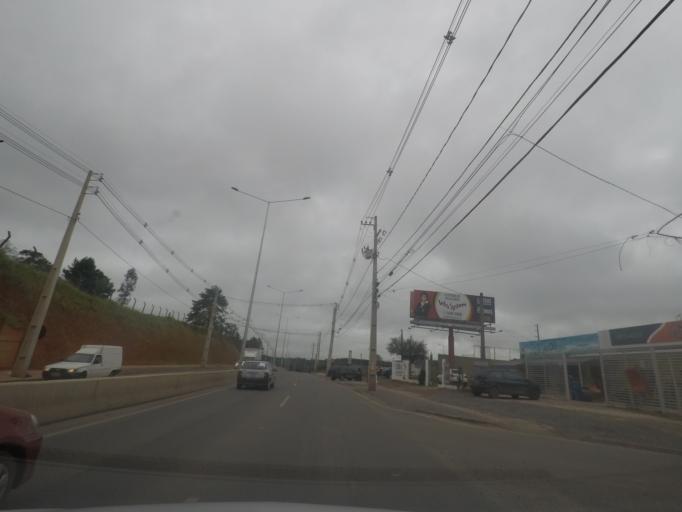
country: BR
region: Parana
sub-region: Piraquara
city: Piraquara
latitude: -25.4569
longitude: -49.0787
